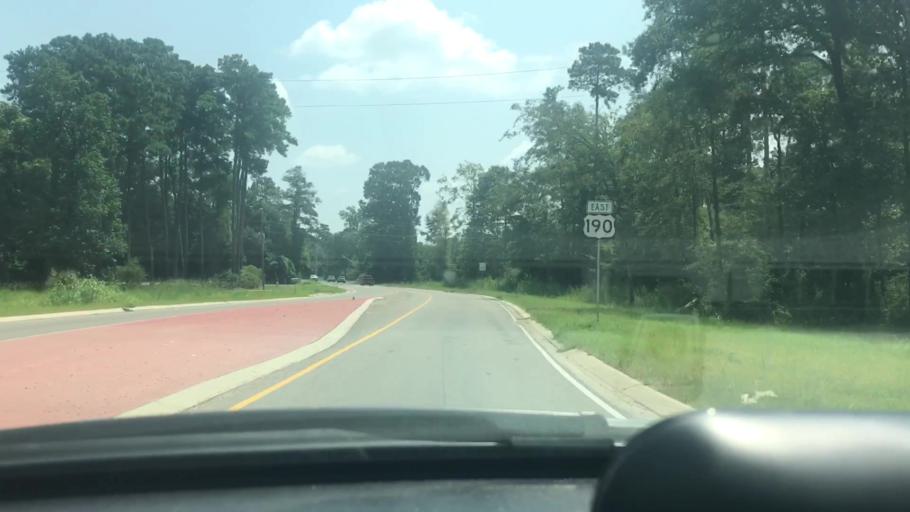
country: US
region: Louisiana
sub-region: Livingston Parish
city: Denham Springs
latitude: 30.4831
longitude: -90.9259
